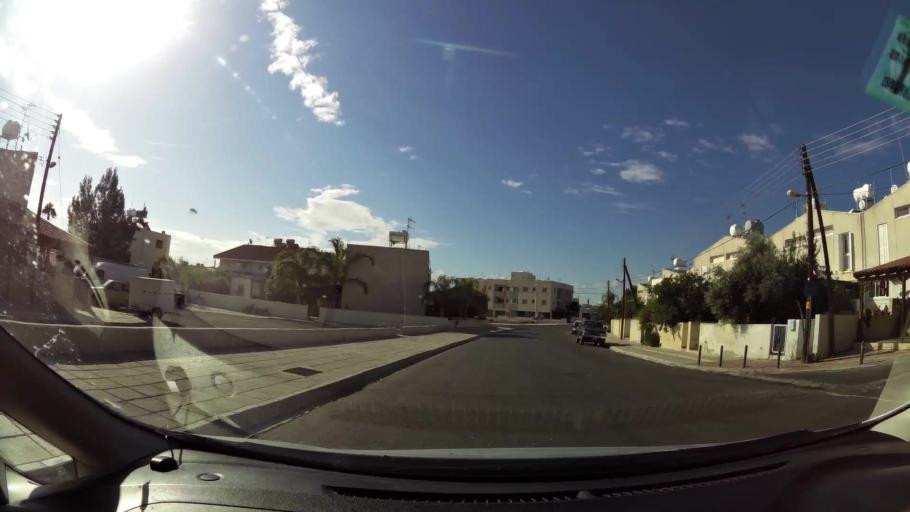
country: CY
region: Lefkosia
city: Nicosia
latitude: 35.1272
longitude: 33.3497
